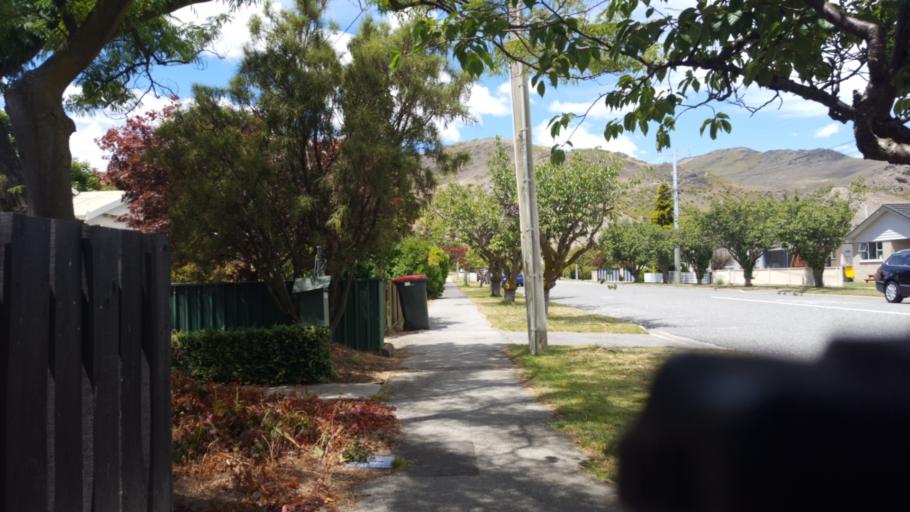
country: NZ
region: Otago
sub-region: Queenstown-Lakes District
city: Wanaka
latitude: -45.0442
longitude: 169.2094
